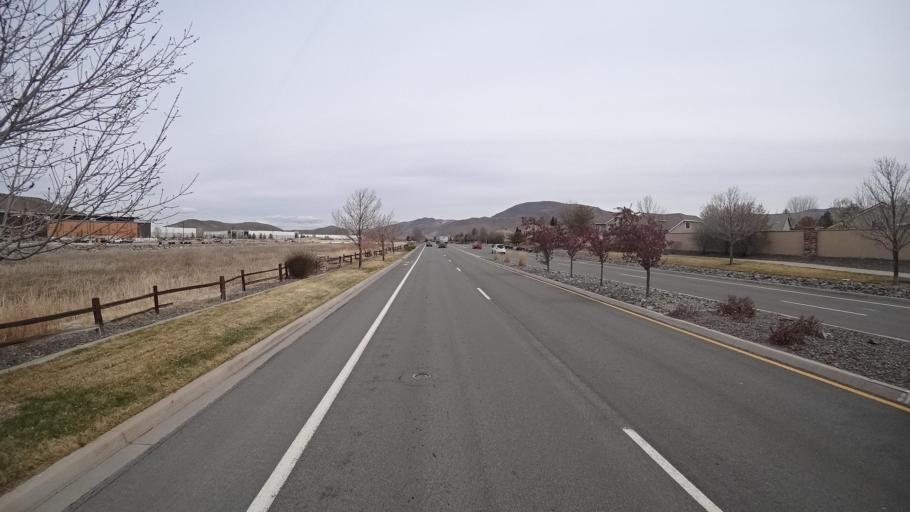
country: US
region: Nevada
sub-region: Washoe County
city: Sparks
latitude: 39.4445
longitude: -119.7444
